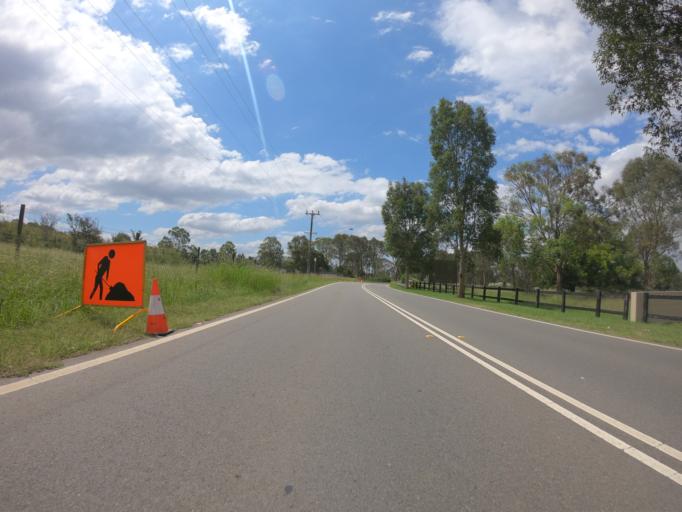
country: AU
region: New South Wales
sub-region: Penrith Municipality
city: Kingswood Park
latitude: -33.8297
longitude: 150.7582
